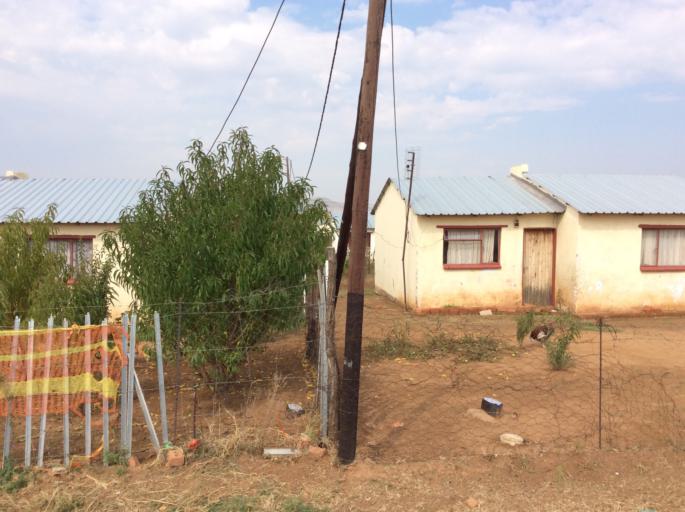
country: LS
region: Mafeteng
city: Mafeteng
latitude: -29.9889
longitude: 27.0014
